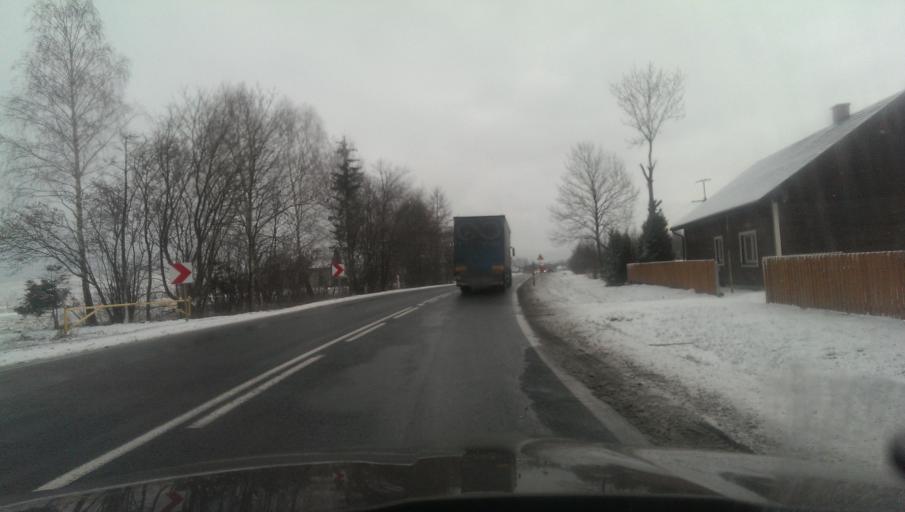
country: PL
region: Subcarpathian Voivodeship
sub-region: Powiat sanocki
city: Nowosielce-Gniewosz
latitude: 49.5643
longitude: 22.1210
